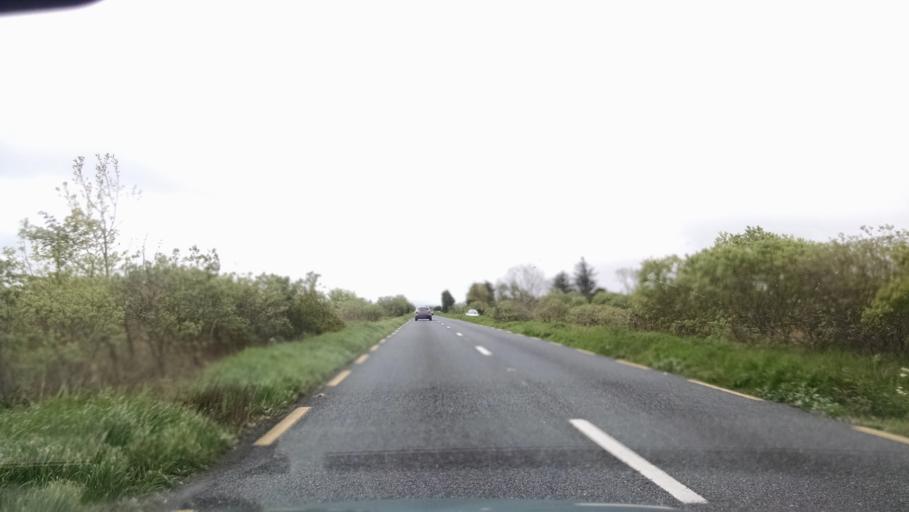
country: IE
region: Connaught
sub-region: County Galway
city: Claregalway
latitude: 53.3451
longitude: -9.0190
